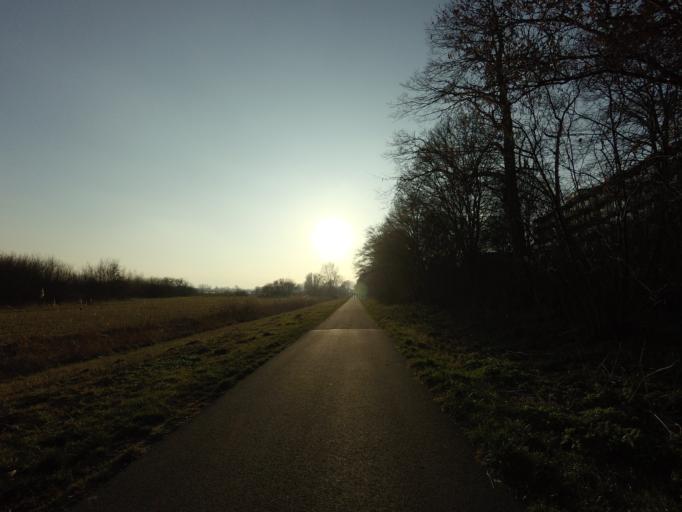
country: NL
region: North Holland
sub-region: Gemeente Haarlem
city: Haarlem
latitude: 52.3519
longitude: 4.6658
